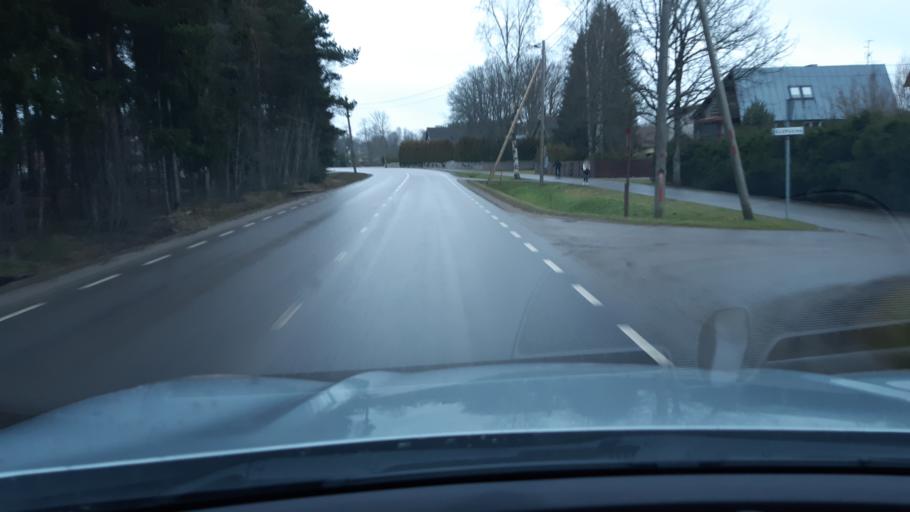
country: EE
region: Harju
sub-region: Saku vald
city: Saku
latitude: 59.2425
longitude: 24.6802
